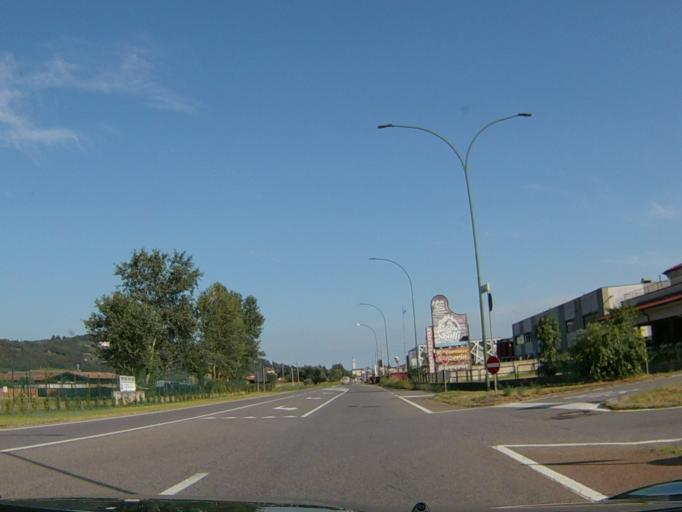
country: IT
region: Lombardy
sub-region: Provincia di Brescia
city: Coccaglio
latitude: 45.5707
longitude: 9.9583
